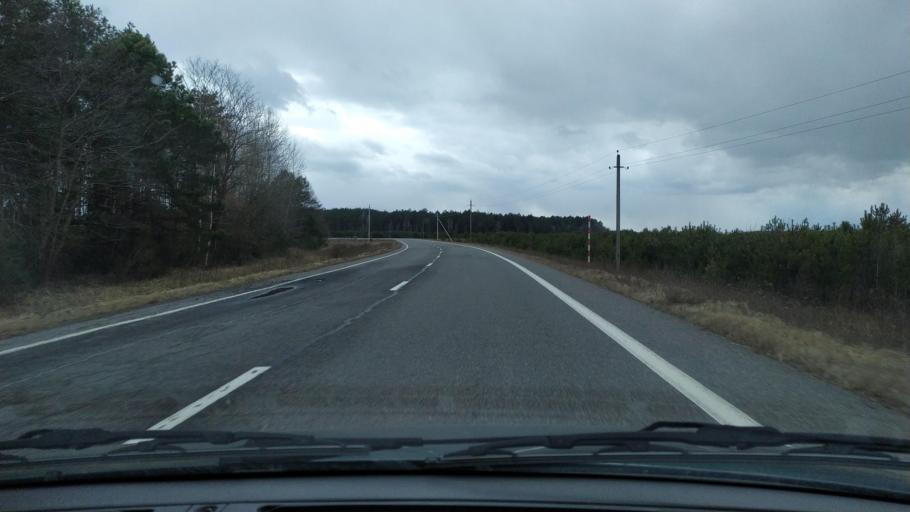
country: BY
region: Brest
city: Kamyanyets
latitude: 52.4014
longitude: 24.0009
